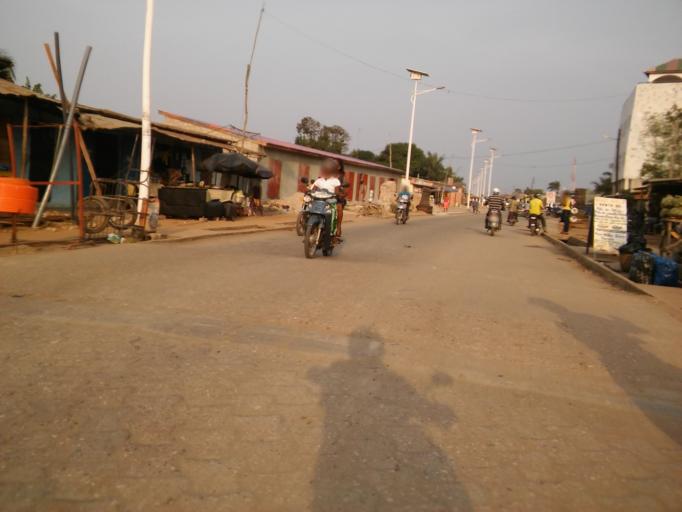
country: BJ
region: Atlantique
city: Abomey-Calavi
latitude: 6.4028
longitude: 2.3341
